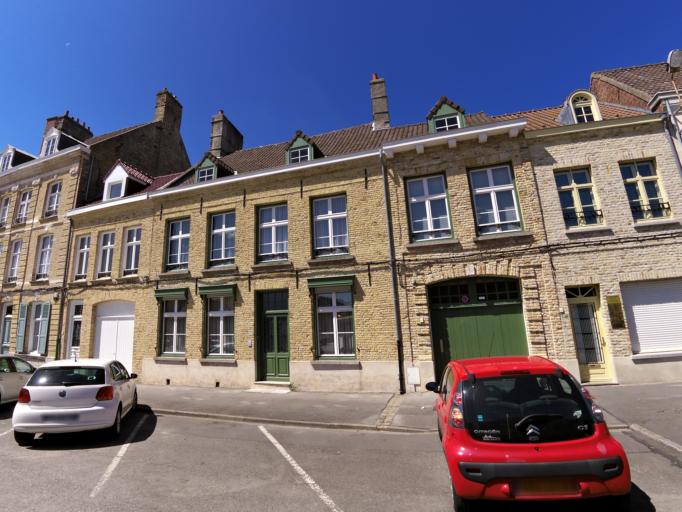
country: FR
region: Nord-Pas-de-Calais
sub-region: Departement du Nord
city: Bergues
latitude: 50.9670
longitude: 2.4338
